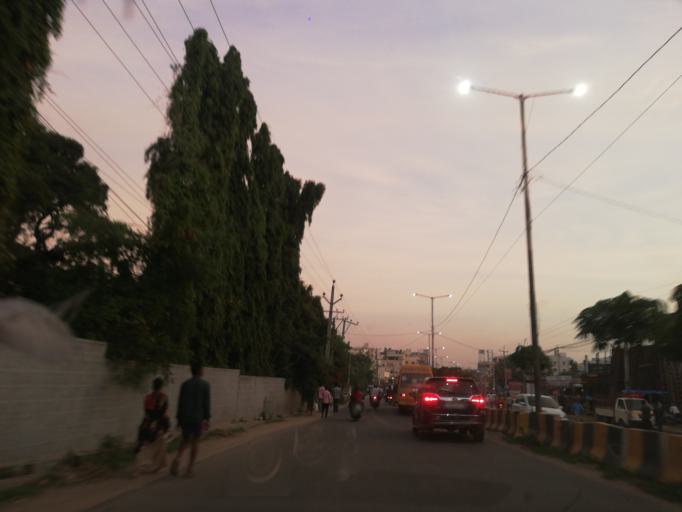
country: IN
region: Telangana
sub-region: Rangareddi
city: Kukatpalli
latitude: 17.5016
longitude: 78.3622
